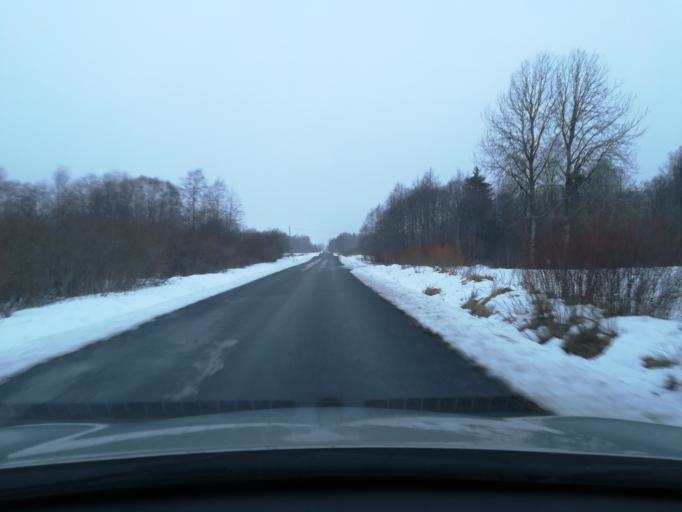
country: EE
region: Harju
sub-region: Raasiku vald
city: Raasiku
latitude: 59.3391
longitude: 25.2323
